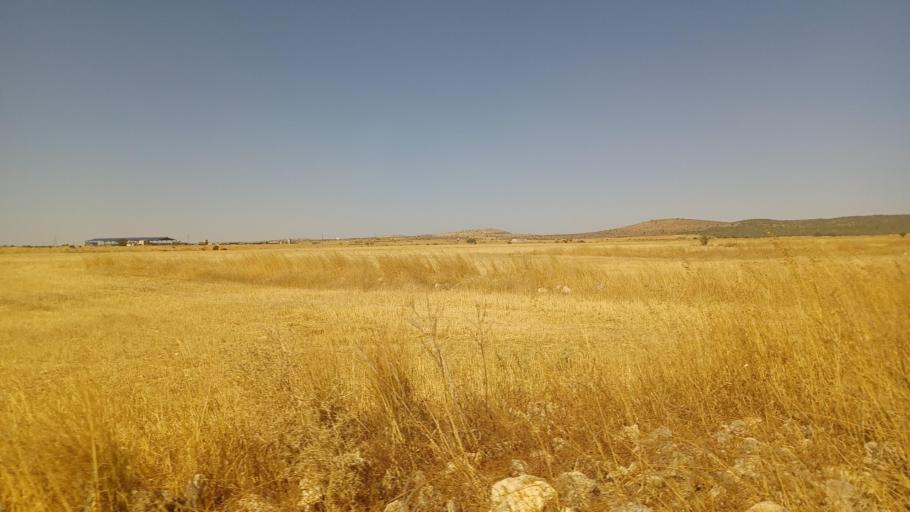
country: CY
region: Larnaka
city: Pergamos
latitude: 35.0399
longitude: 33.6888
